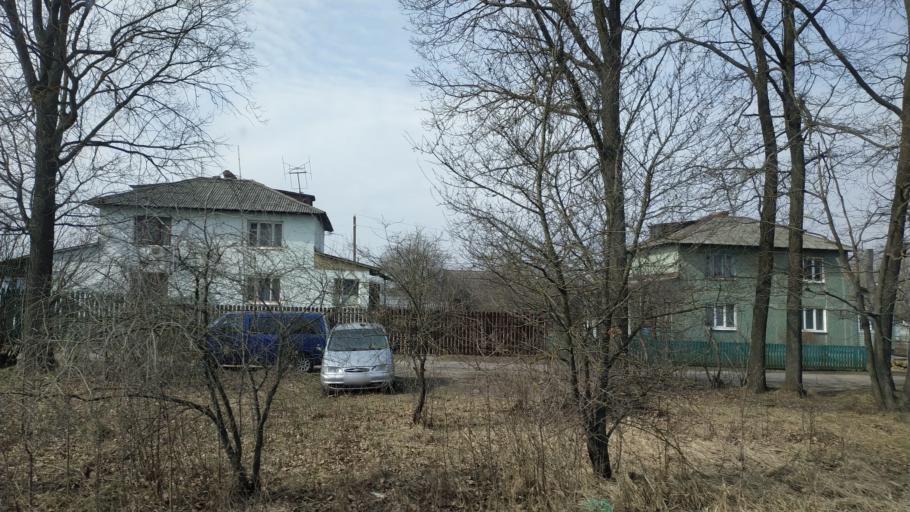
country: RU
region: Moskovskaya
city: Bronnitsy
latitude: 55.3886
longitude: 38.3491
